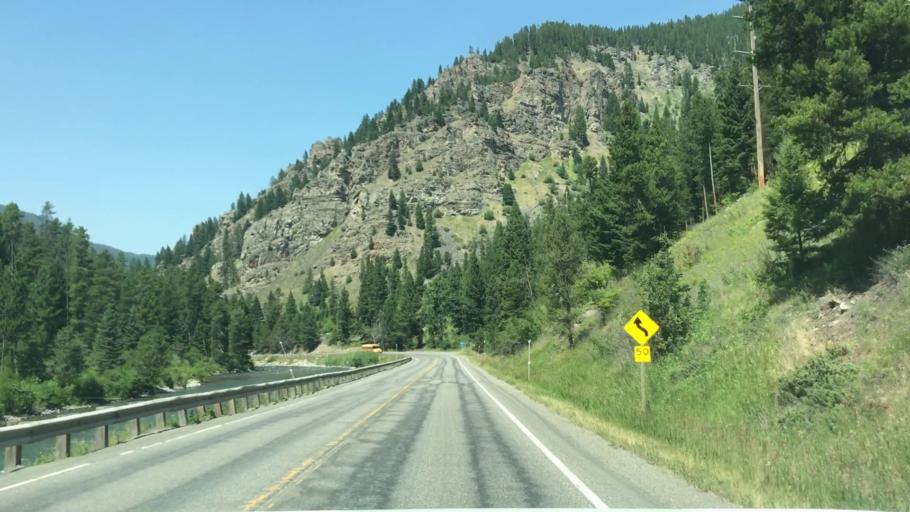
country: US
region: Montana
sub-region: Gallatin County
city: Big Sky
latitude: 45.3930
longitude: -111.2054
